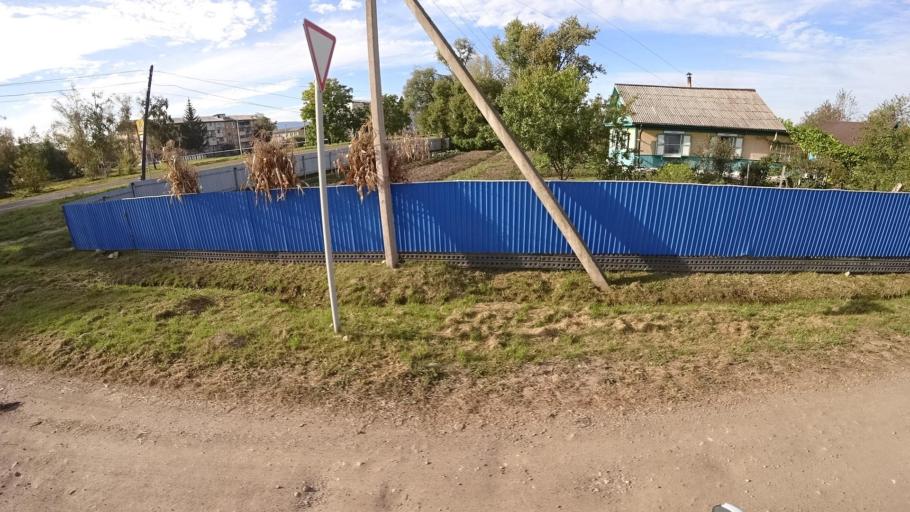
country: RU
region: Primorskiy
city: Dostoyevka
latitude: 44.2898
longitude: 133.4268
